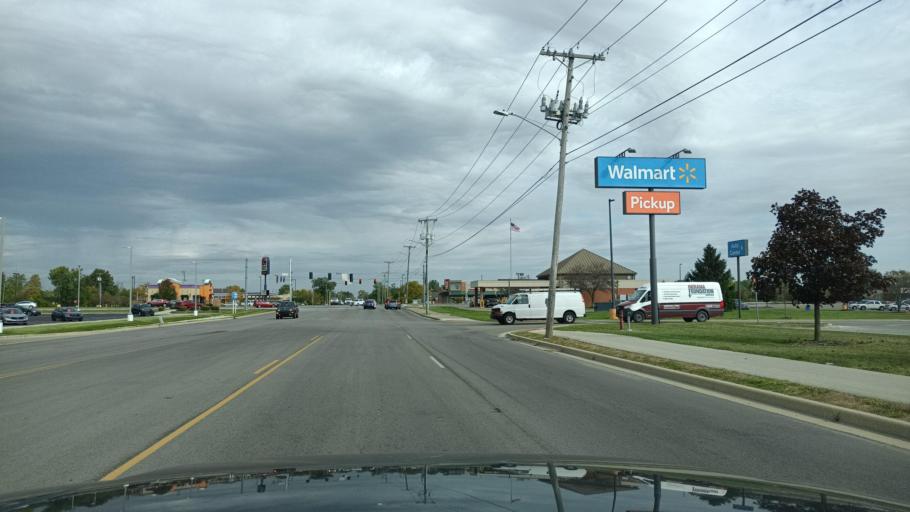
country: US
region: Indiana
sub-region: Delaware County
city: Muncie
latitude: 40.2169
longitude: -85.4426
